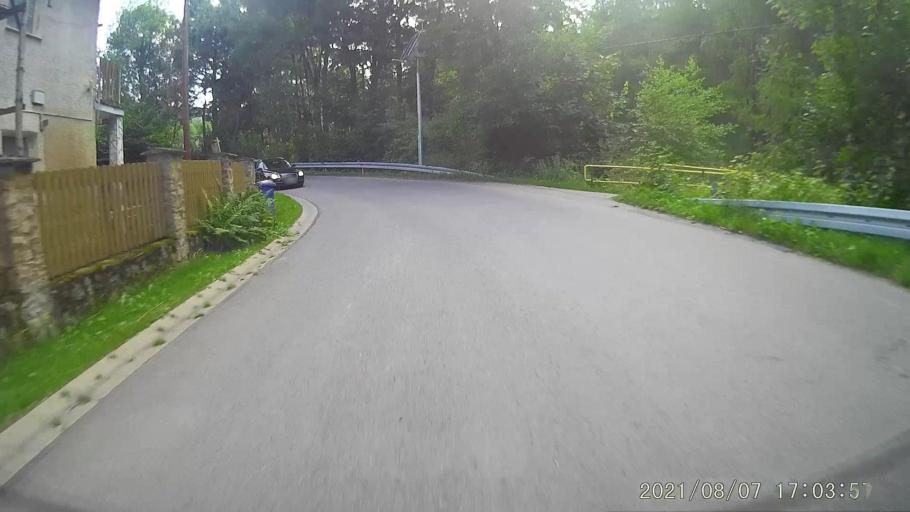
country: PL
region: Lower Silesian Voivodeship
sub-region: Powiat klodzki
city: Bystrzyca Klodzka
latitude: 50.2924
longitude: 16.5646
